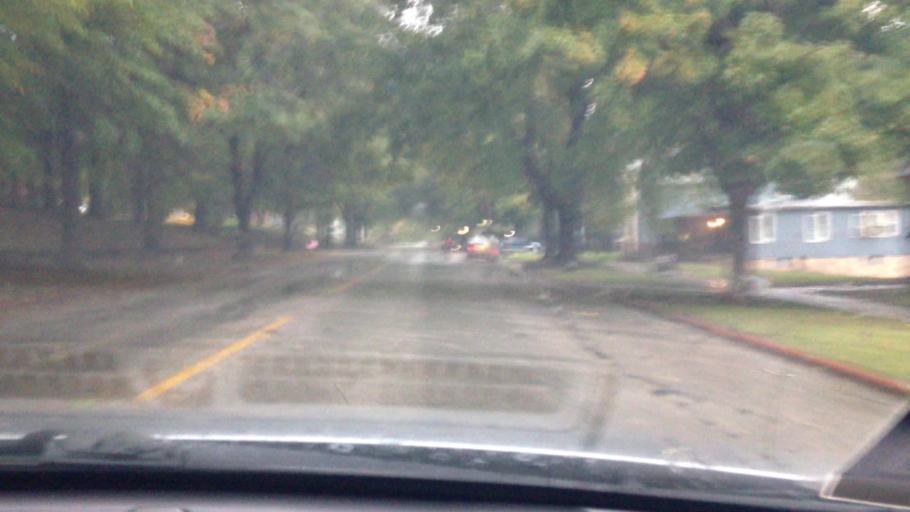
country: US
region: Kansas
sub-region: Leavenworth County
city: Leavenworth
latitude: 39.3226
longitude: -94.9224
